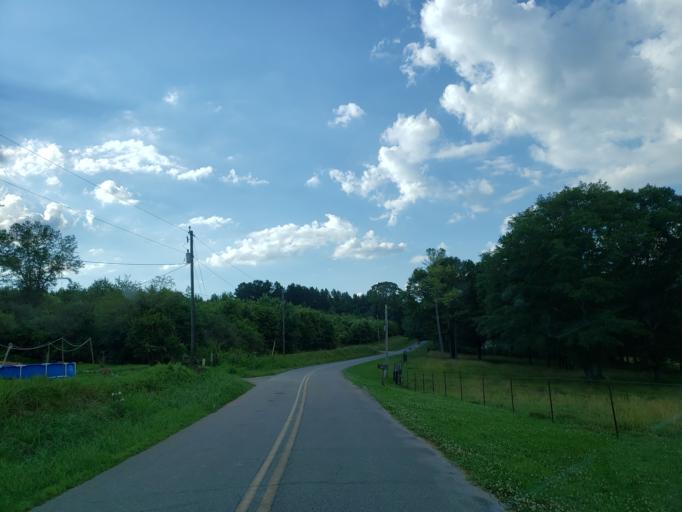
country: US
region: Georgia
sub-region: Polk County
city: Cedartown
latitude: 33.9212
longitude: -85.2700
